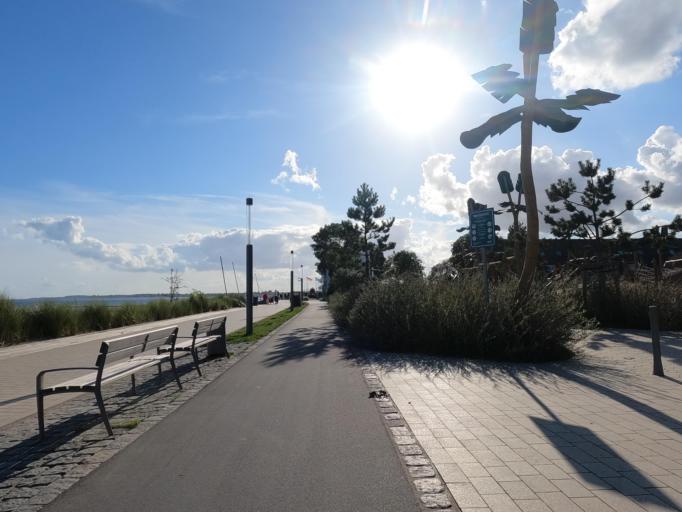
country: DE
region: Schleswig-Holstein
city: Grossenbrode
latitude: 54.3546
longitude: 11.0836
